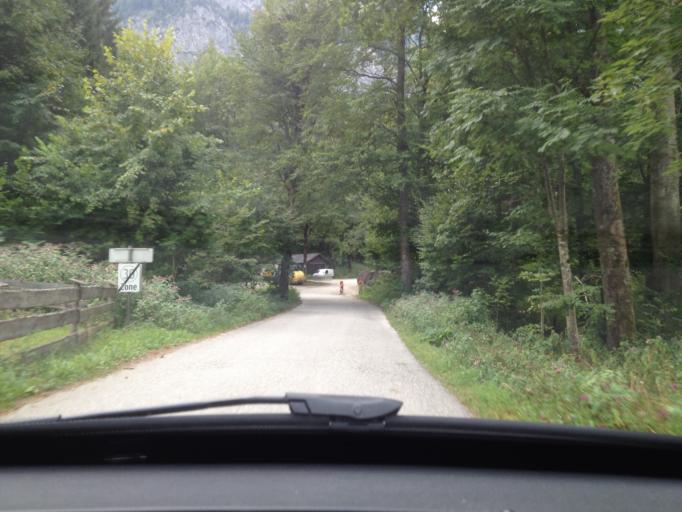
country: AT
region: Upper Austria
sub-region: Politischer Bezirk Gmunden
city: Bad Goisern
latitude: 47.6240
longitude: 13.6142
